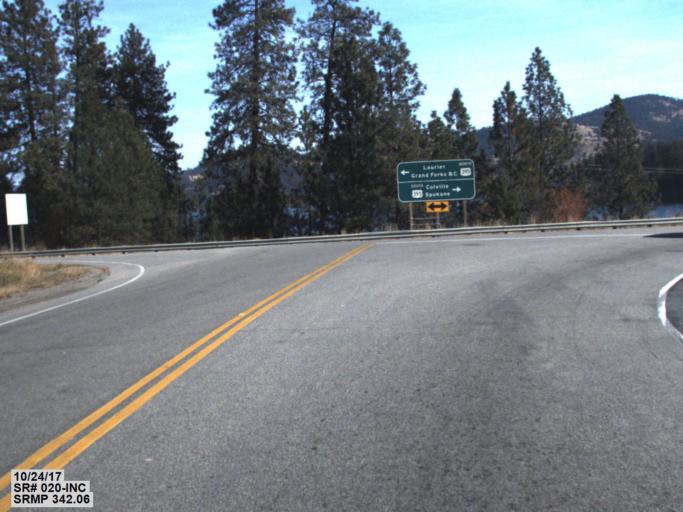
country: US
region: Washington
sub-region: Stevens County
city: Kettle Falls
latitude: 48.6273
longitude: -118.1231
